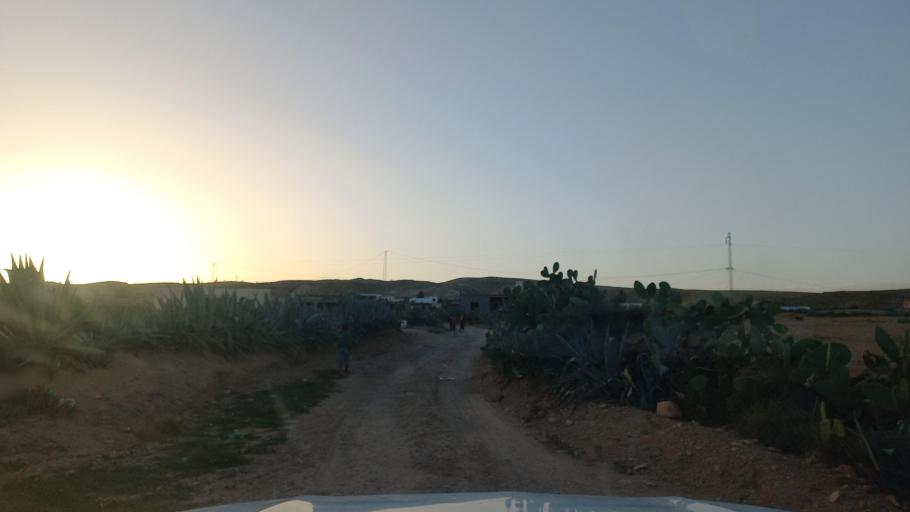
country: TN
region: Al Qasrayn
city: Sbiba
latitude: 35.3750
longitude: 9.0124
